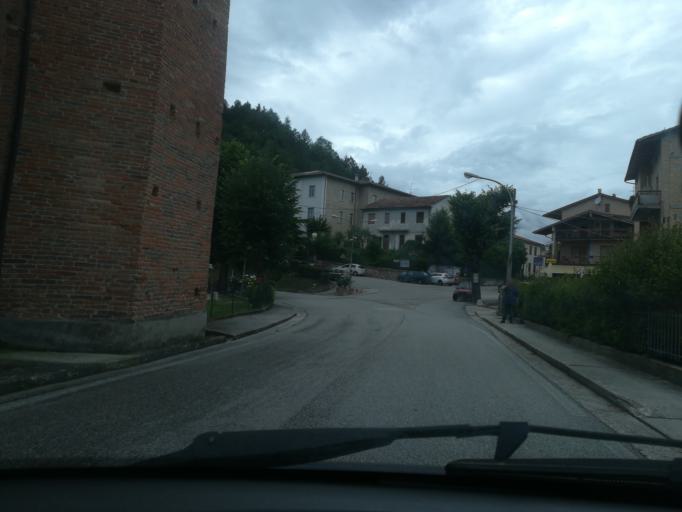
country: IT
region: The Marches
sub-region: Province of Fermo
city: Montefortino
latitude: 42.9429
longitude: 13.3456
